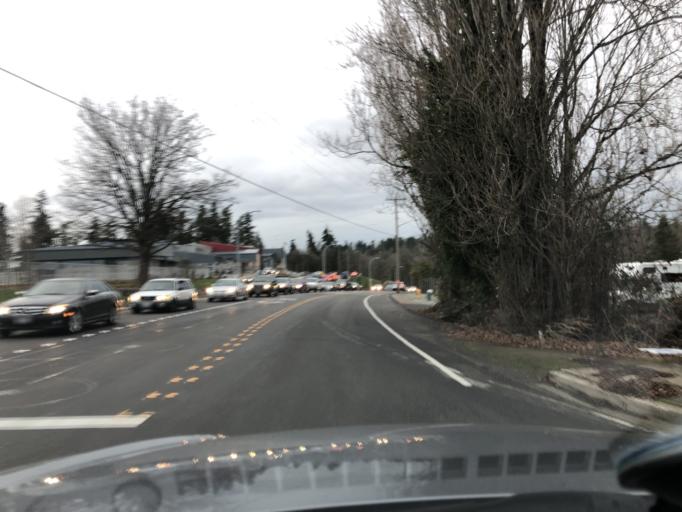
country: US
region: Washington
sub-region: King County
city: Des Moines
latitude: 47.3868
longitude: -122.3131
